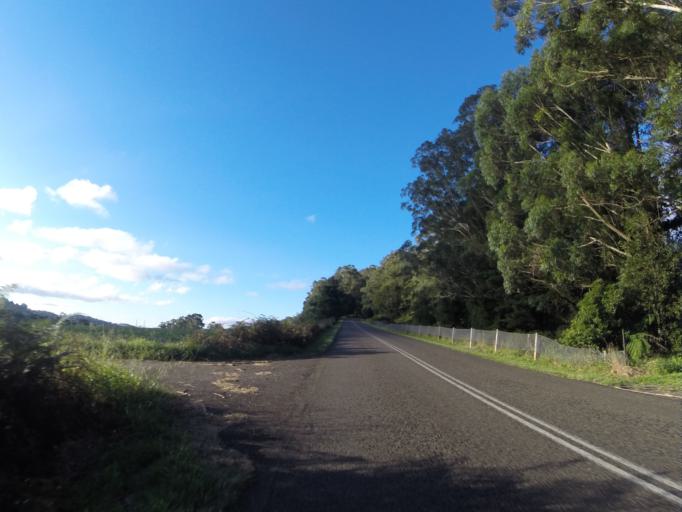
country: AU
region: New South Wales
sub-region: Shoalhaven Shire
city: Kangaroo Valley
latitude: -34.6441
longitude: 150.5118
